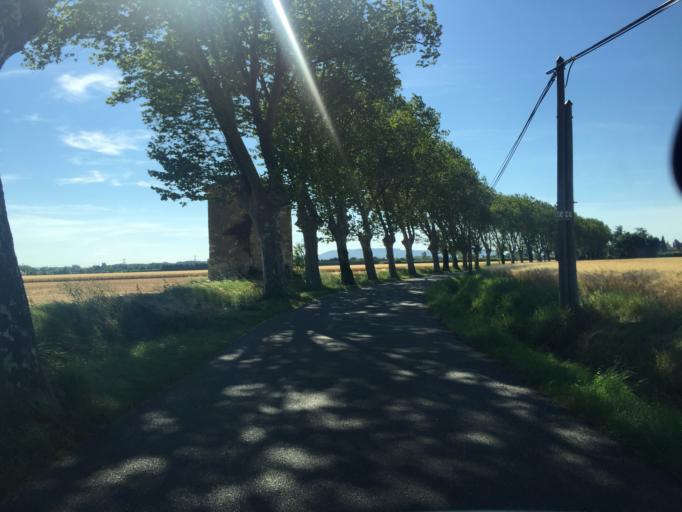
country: FR
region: Provence-Alpes-Cote d'Azur
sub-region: Departement du Vaucluse
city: Caderousse
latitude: 44.1061
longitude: 4.7513
